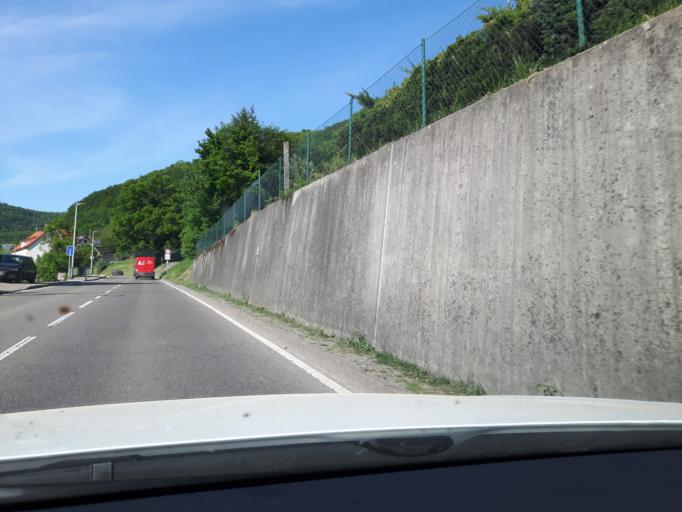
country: DE
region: Baden-Wuerttemberg
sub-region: Tuebingen Region
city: Pfullingen
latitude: 48.4328
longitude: 9.2592
